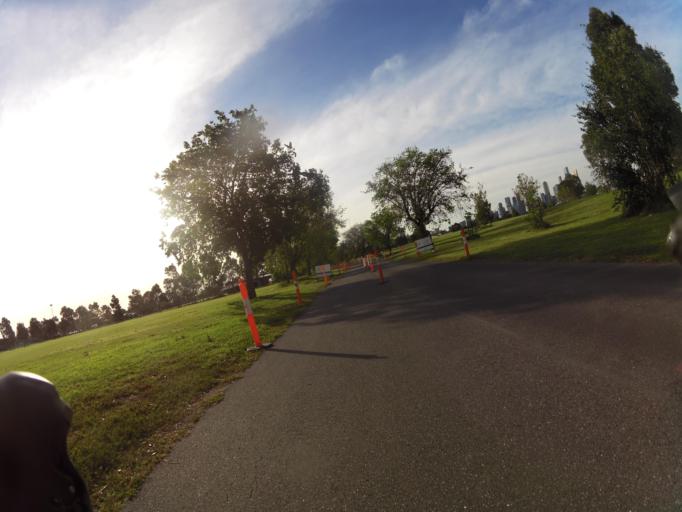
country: AU
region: Victoria
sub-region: Port Phillip
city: Middle Park
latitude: -37.8484
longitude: 144.9700
